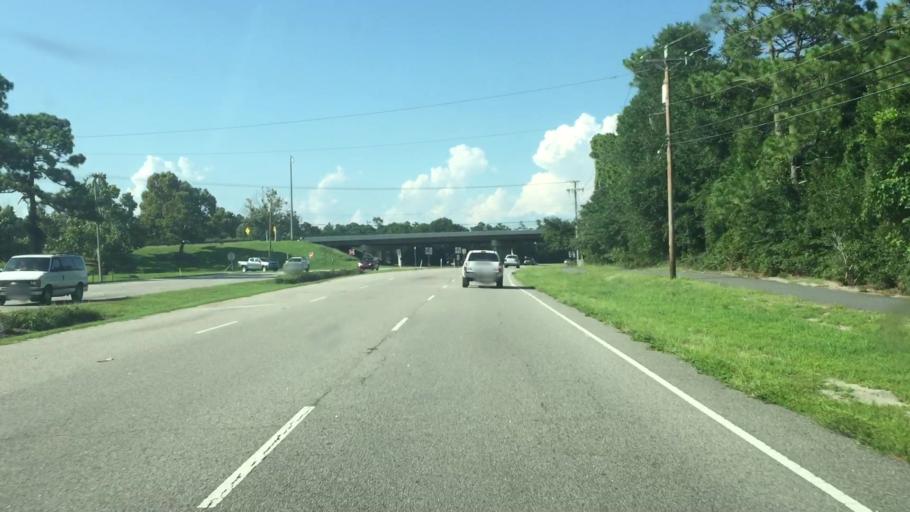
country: US
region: South Carolina
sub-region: Horry County
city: Myrtle Beach
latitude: 33.7656
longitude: -78.8056
